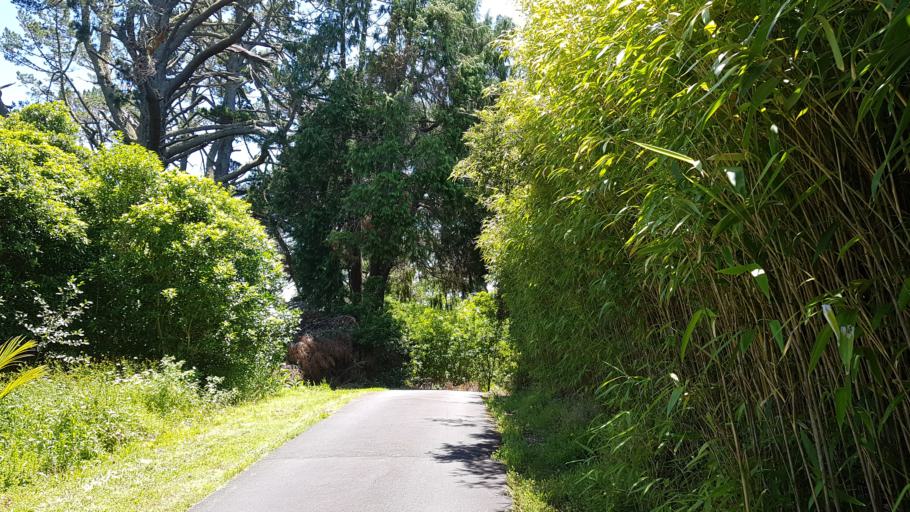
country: NZ
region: Auckland
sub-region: Auckland
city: North Shore
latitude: -36.8216
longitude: 174.7191
